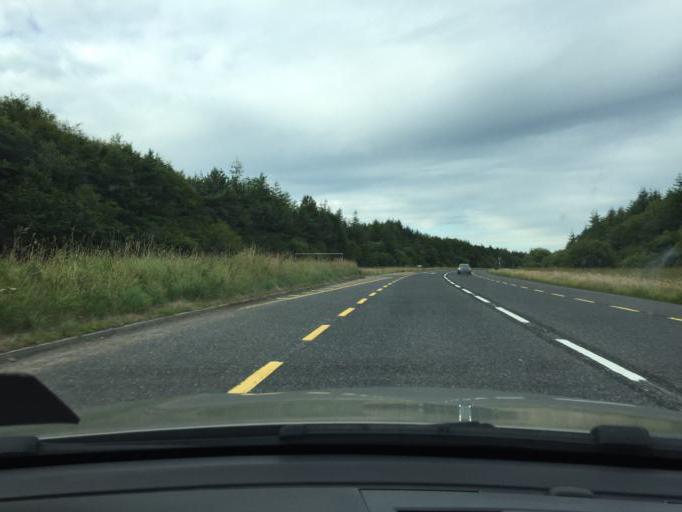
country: IE
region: Munster
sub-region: Waterford
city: Dungarvan
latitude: 52.0253
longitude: -7.6808
